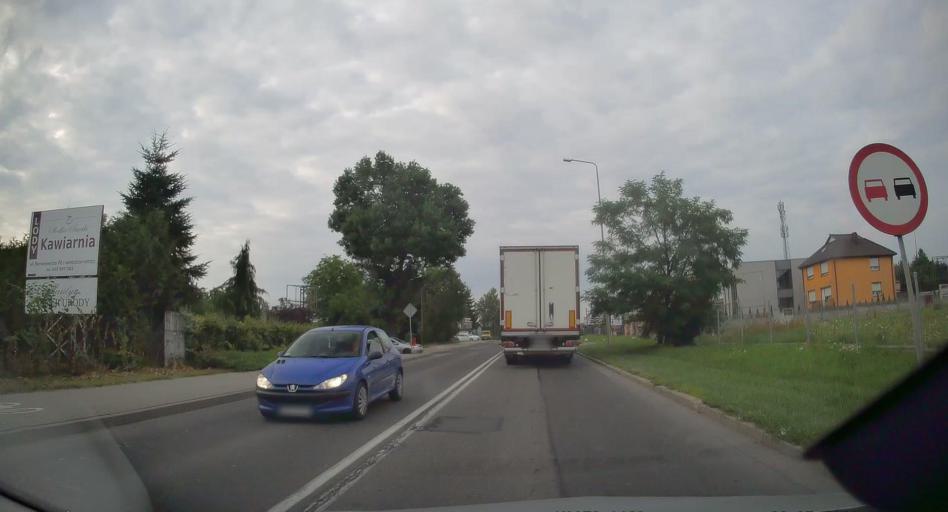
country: PL
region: Lodz Voivodeship
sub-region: Powiat radomszczanski
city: Radomsko
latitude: 51.0542
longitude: 19.4402
